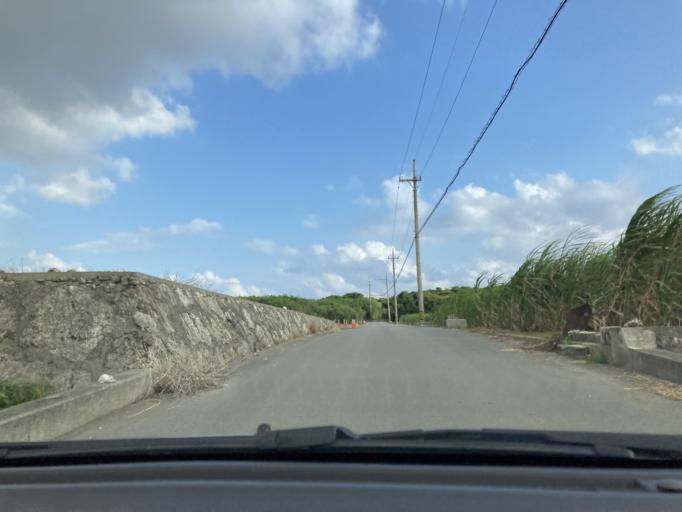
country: JP
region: Okinawa
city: Itoman
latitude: 26.0829
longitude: 127.6681
